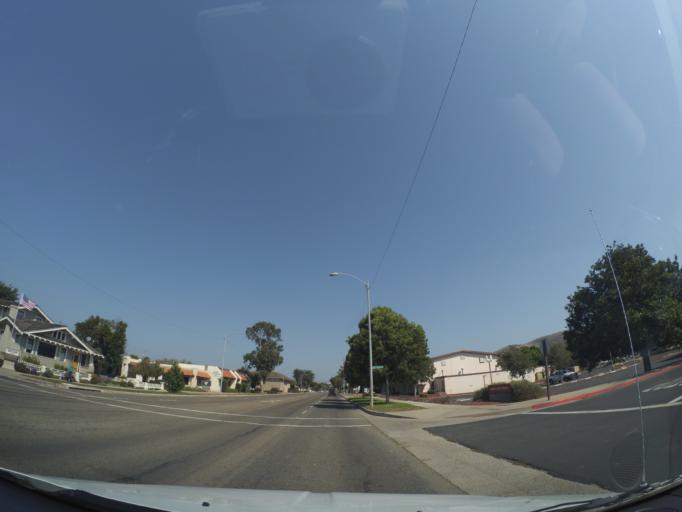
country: US
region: California
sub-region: Santa Barbara County
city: Lompoc
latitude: 34.6389
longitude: -120.4530
